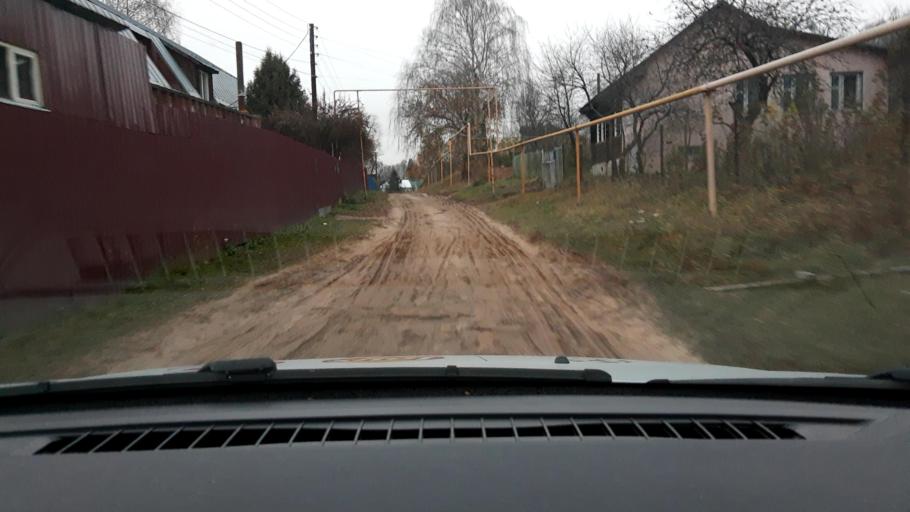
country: RU
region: Nizjnij Novgorod
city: Neklyudovo
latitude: 56.4222
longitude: 44.0174
